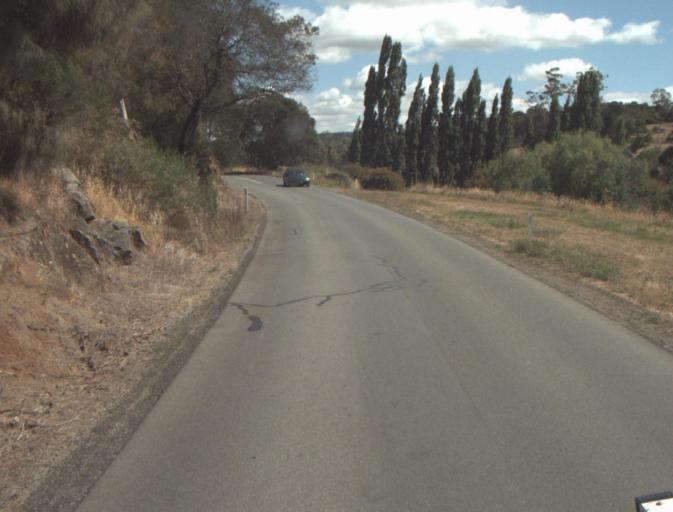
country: AU
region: Tasmania
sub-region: Launceston
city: Newstead
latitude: -41.4150
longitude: 147.1644
